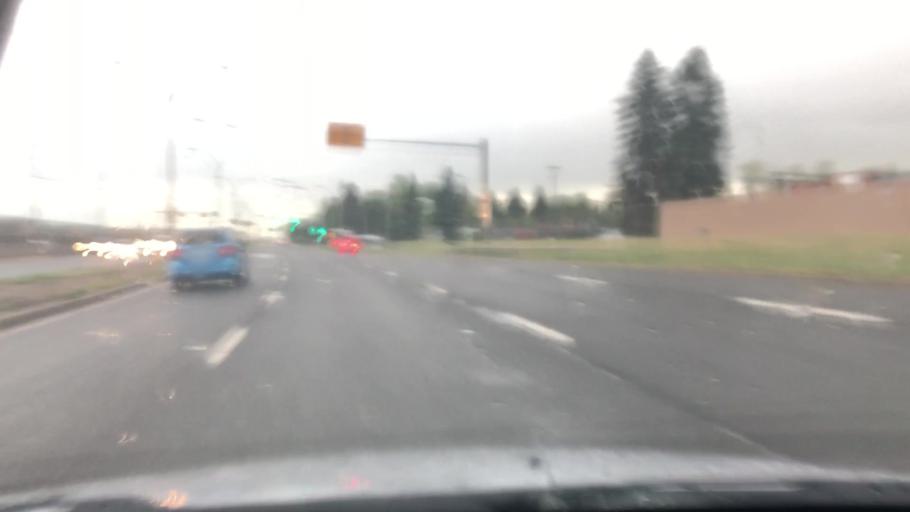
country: CA
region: Alberta
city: Edmonton
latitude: 53.5813
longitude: -113.5079
